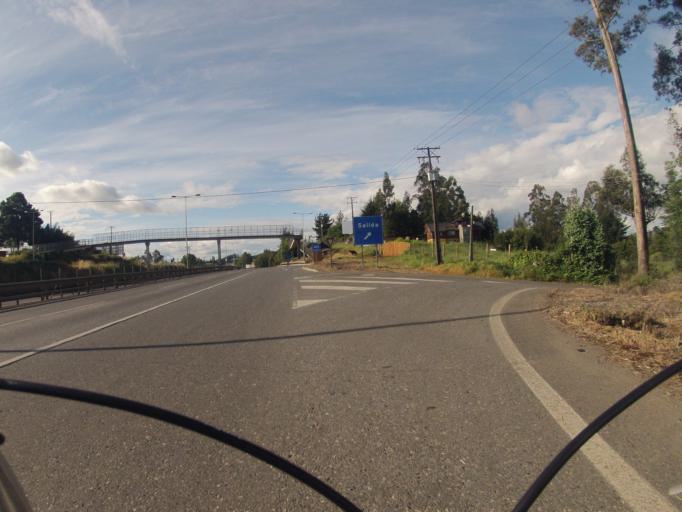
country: CL
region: Araucania
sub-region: Provincia de Cautin
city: Temuco
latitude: -38.8201
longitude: -72.6233
